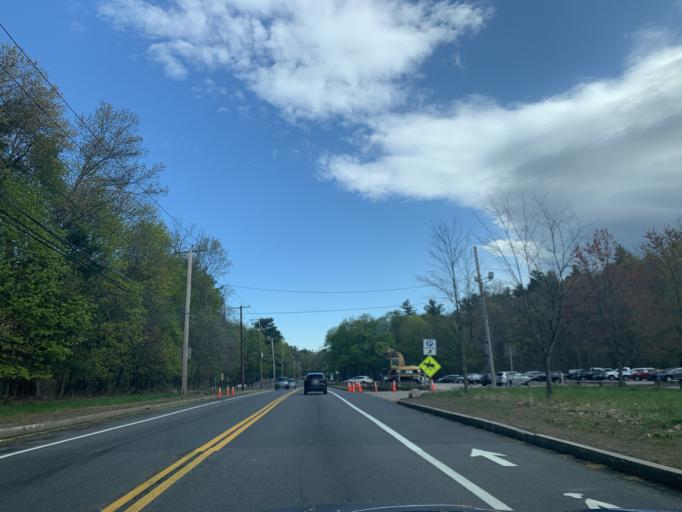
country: US
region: Massachusetts
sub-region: Norfolk County
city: Dedham
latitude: 42.2191
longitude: -71.1192
